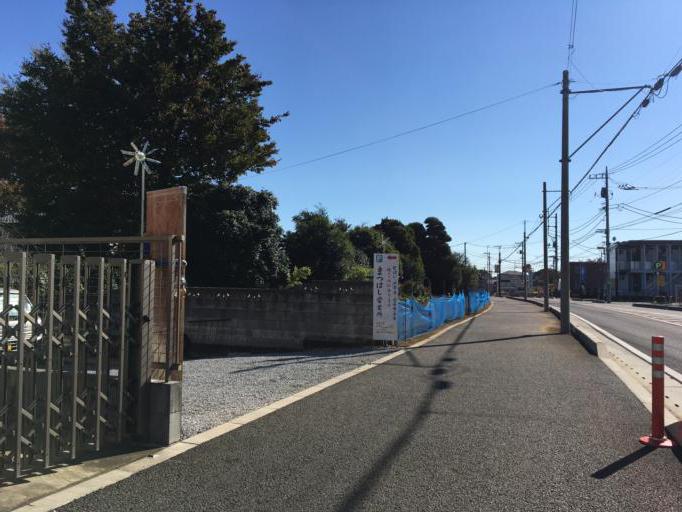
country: JP
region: Saitama
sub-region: Kawaguchi-shi
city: Hatogaya-honcho
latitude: 35.8424
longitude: 139.7361
